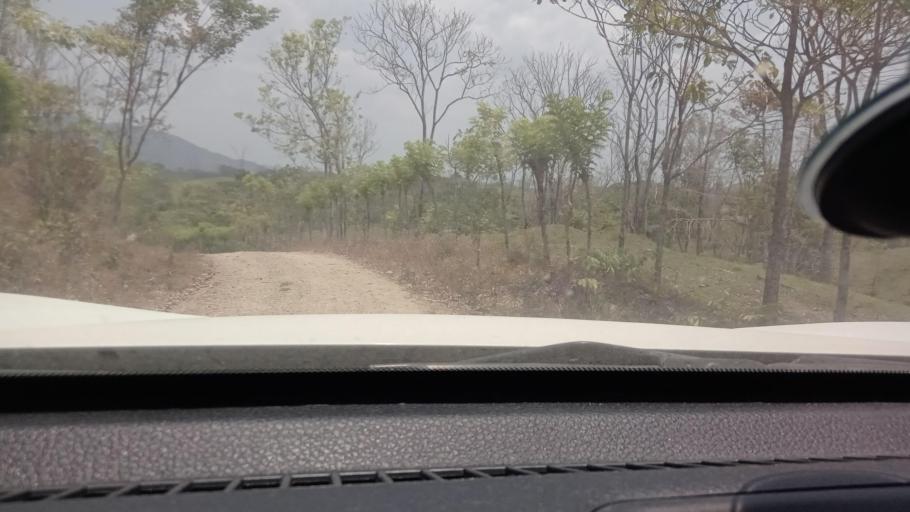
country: MX
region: Tabasco
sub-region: Huimanguillo
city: Francisco Rueda
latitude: 17.4883
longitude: -93.9326
